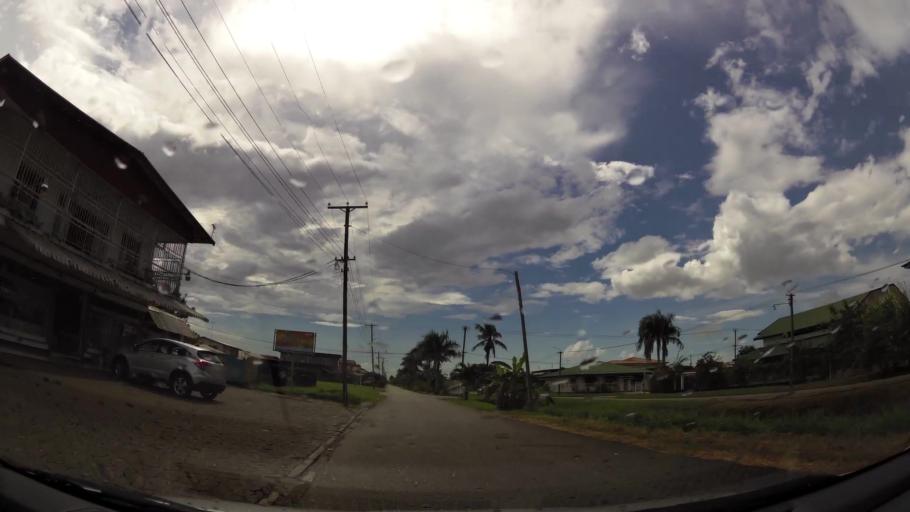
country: SR
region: Paramaribo
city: Paramaribo
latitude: 5.8383
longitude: -55.1312
